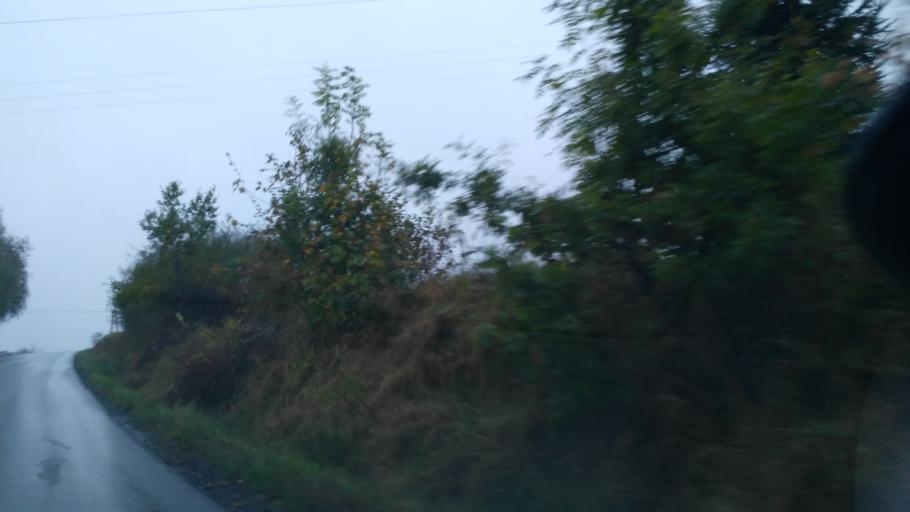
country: PL
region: Subcarpathian Voivodeship
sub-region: Powiat krosnienski
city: Kroscienko Wyzne
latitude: 49.6848
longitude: 21.8110
